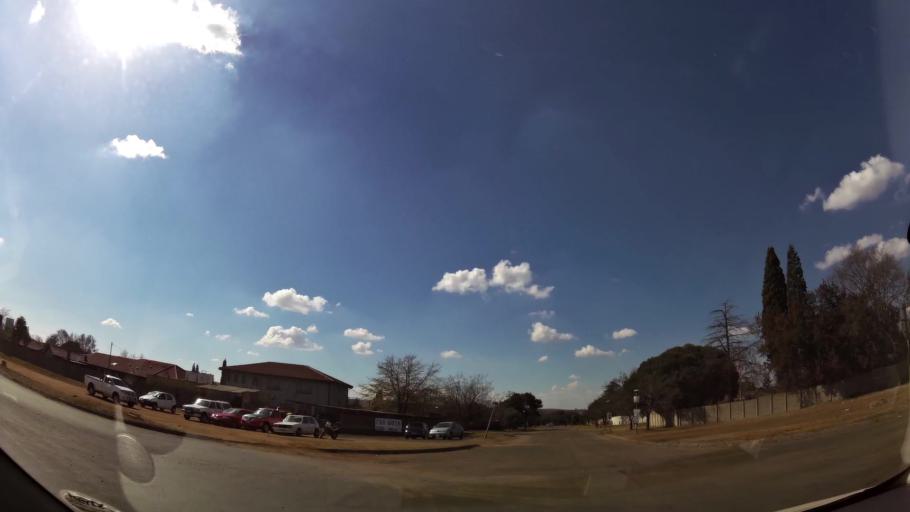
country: ZA
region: Mpumalanga
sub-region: Nkangala District Municipality
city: Witbank
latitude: -25.9461
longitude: 29.2455
